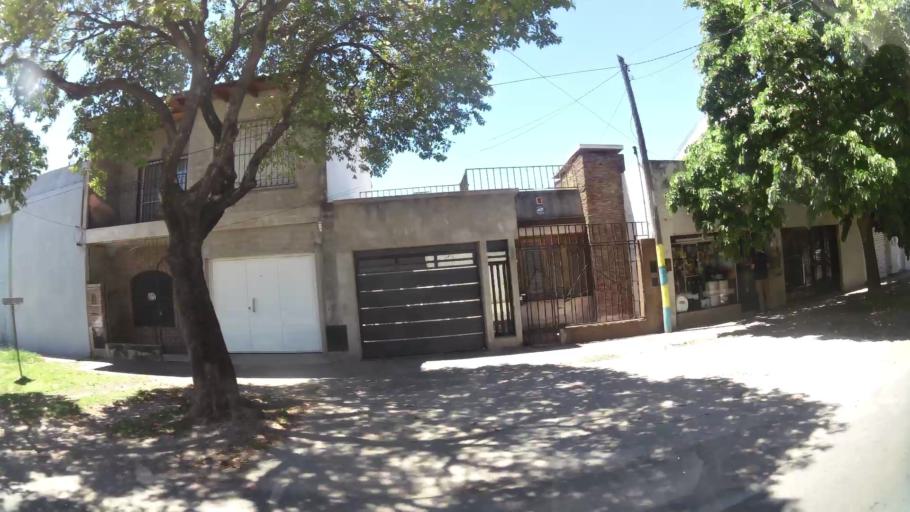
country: AR
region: Santa Fe
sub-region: Departamento de Rosario
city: Rosario
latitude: -32.9582
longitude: -60.7049
